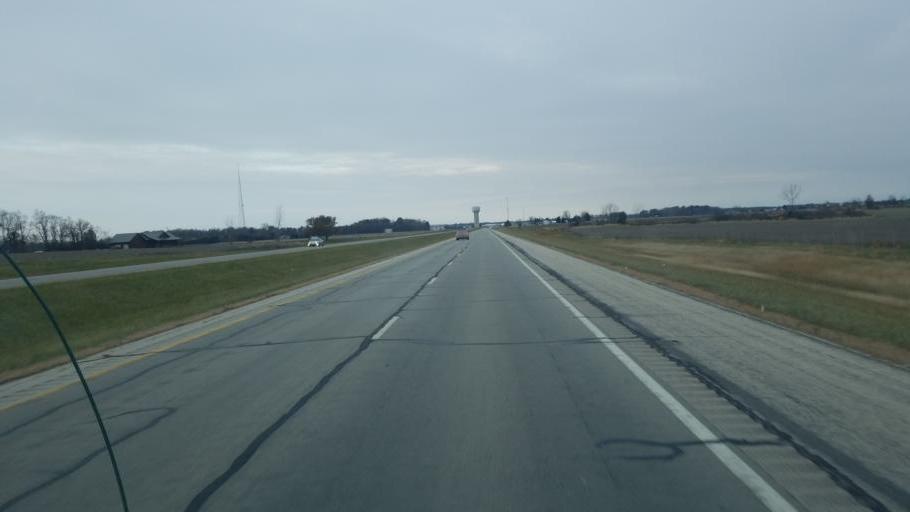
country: US
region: Ohio
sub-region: Mercer County
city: Celina
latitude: 40.5573
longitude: -84.5006
